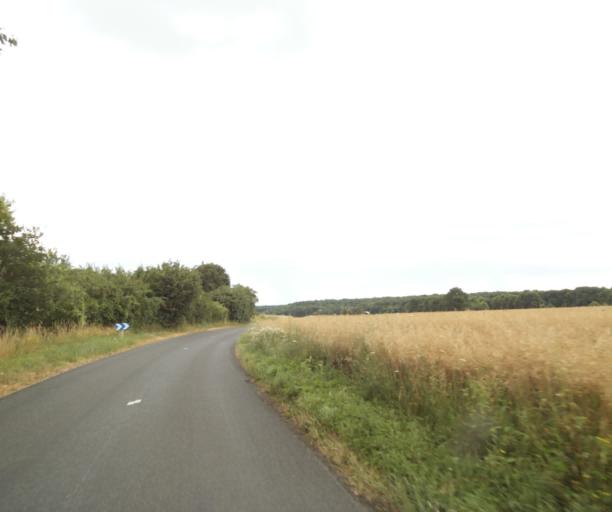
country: FR
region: Ile-de-France
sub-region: Departement de Seine-et-Marne
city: Perthes
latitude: 48.4847
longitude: 2.5486
